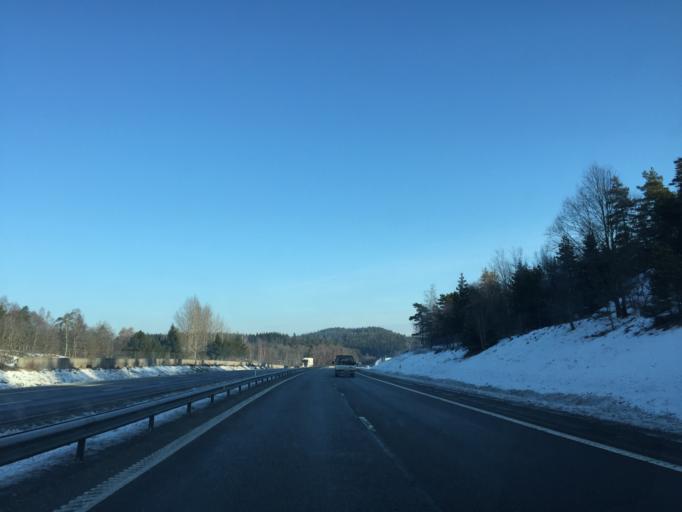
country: SE
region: Vaestra Goetaland
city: Svanesund
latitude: 58.1636
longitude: 11.8890
